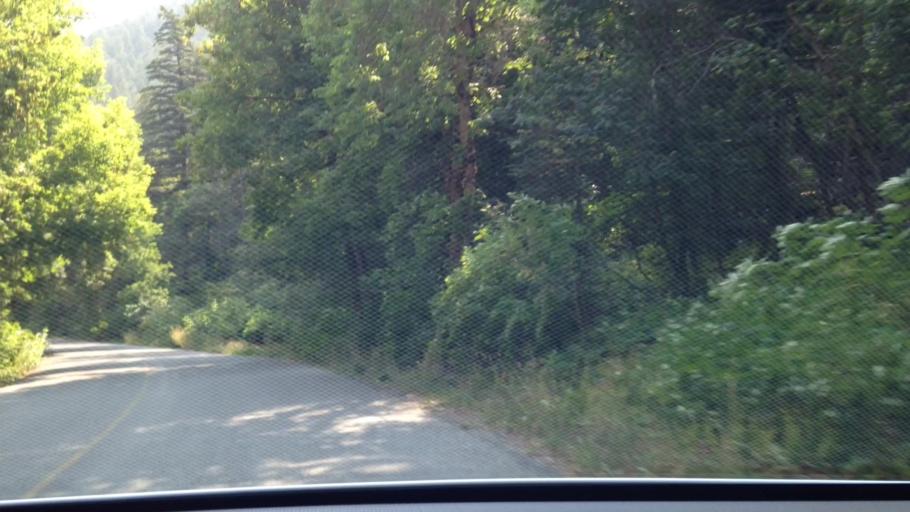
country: US
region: Utah
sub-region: Salt Lake County
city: Mount Olympus
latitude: 40.6993
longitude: -111.7088
